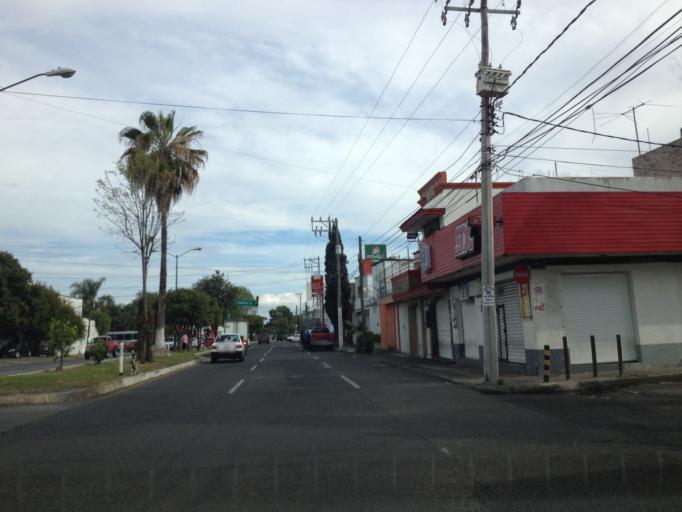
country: MX
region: Michoacan
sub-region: Uruapan
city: Uruapan
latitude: 19.4054
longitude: -102.0505
